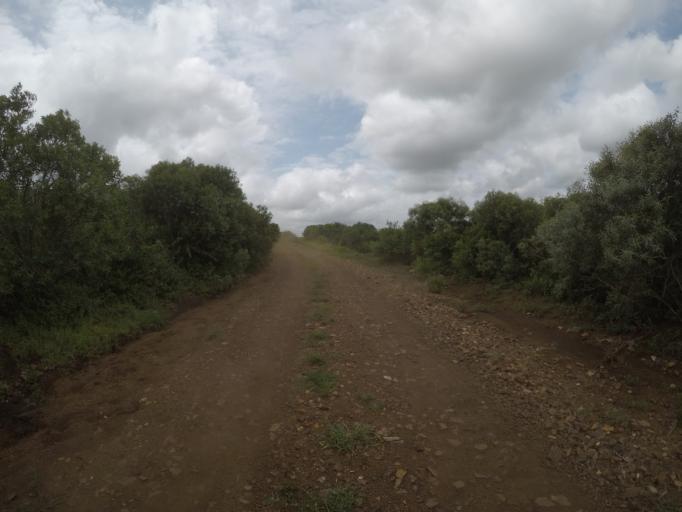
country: ZA
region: KwaZulu-Natal
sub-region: uThungulu District Municipality
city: Empangeni
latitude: -28.5843
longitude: 31.8681
